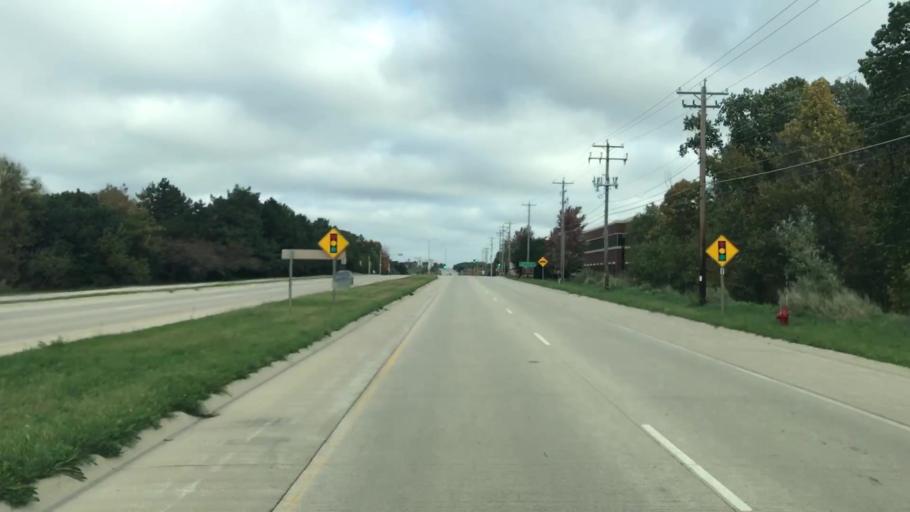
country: US
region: Wisconsin
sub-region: Waukesha County
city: Pewaukee
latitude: 43.0582
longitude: -88.2252
